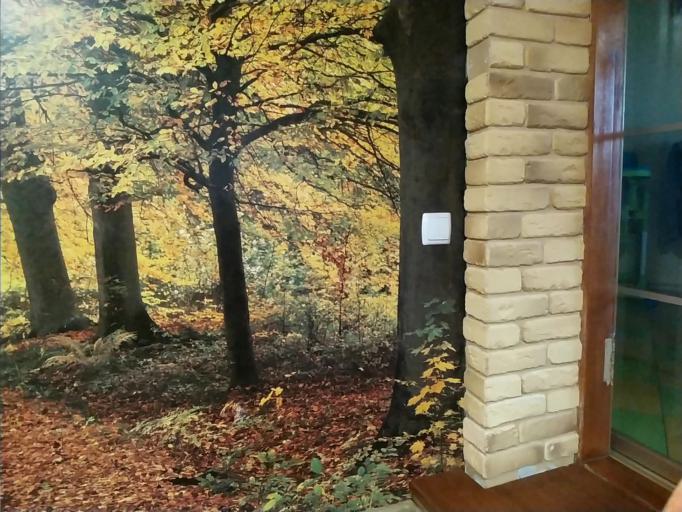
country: RU
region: Smolensk
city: Safonovo
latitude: 55.1925
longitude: 33.1136
